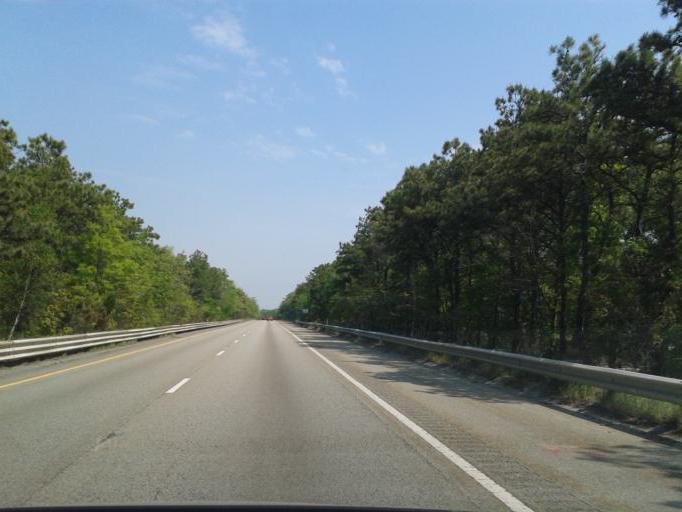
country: US
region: Massachusetts
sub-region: Barnstable County
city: Sagamore
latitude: 41.7908
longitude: -70.5443
